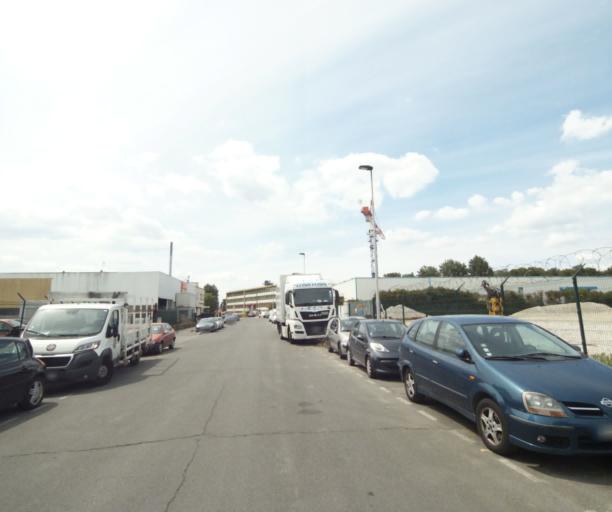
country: FR
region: Ile-de-France
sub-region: Departement du Val-d'Oise
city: Bezons
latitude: 48.9214
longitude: 2.2277
